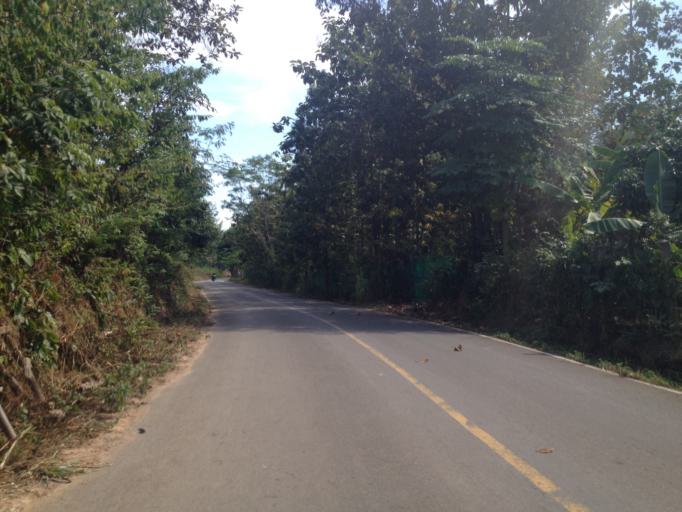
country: TH
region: Chiang Mai
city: Hang Dong
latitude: 18.7154
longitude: 98.8922
